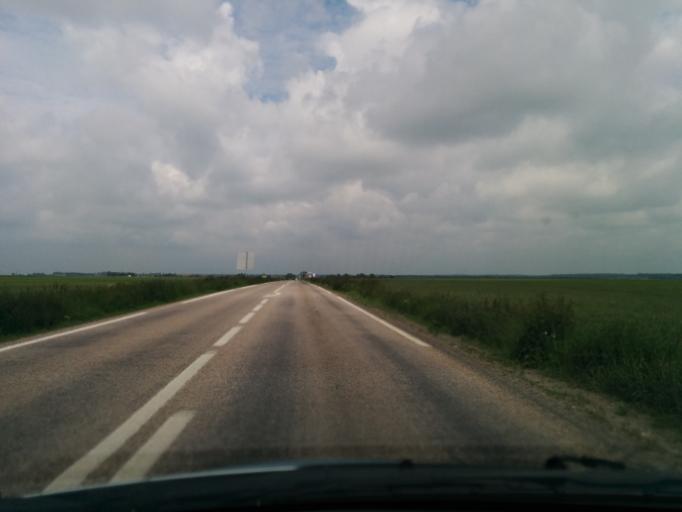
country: FR
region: Ile-de-France
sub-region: Departement des Yvelines
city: Limetz-Villez
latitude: 49.1446
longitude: 1.5389
